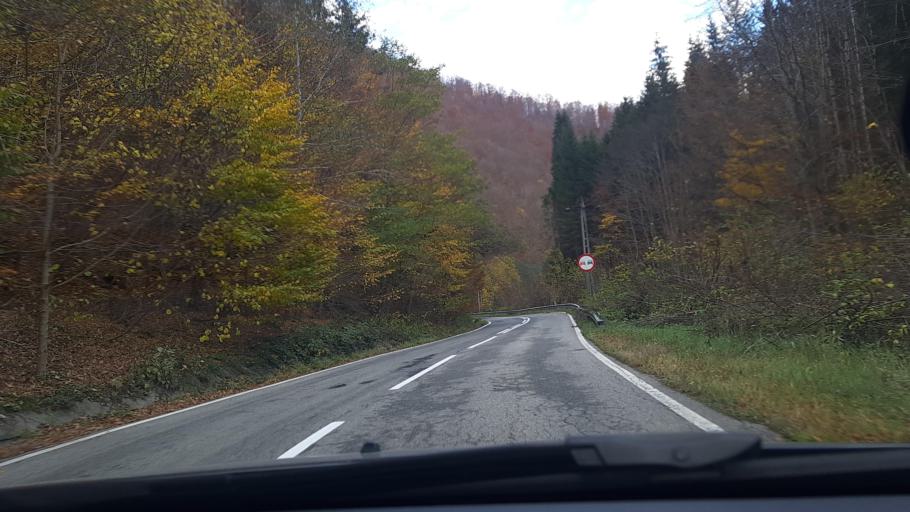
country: RO
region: Valcea
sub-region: Comuna Voineasa
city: Voineasa
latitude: 45.4297
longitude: 23.9048
